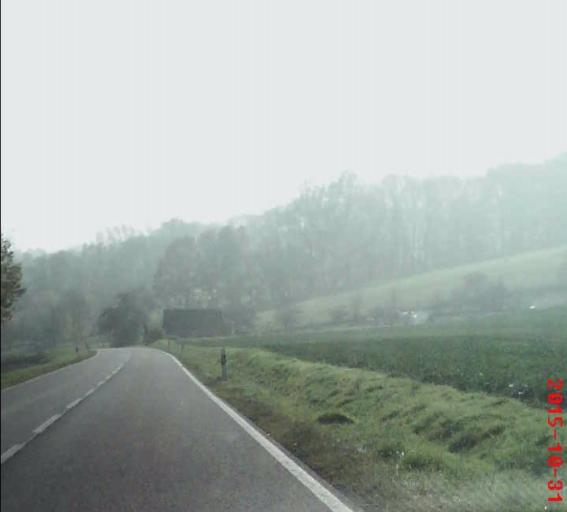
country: DE
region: Thuringia
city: Sickerode
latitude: 51.2579
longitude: 10.1150
